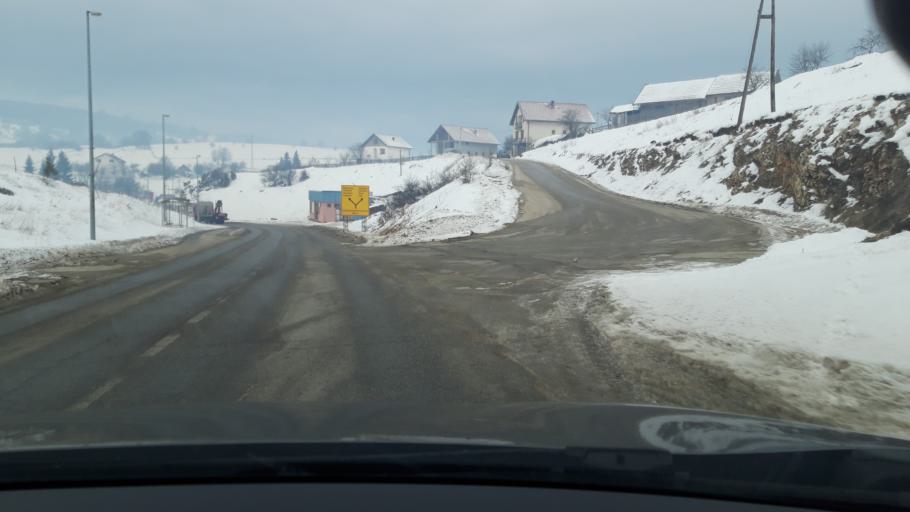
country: BA
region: Republika Srpska
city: Sokolac
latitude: 43.9196
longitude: 18.7705
